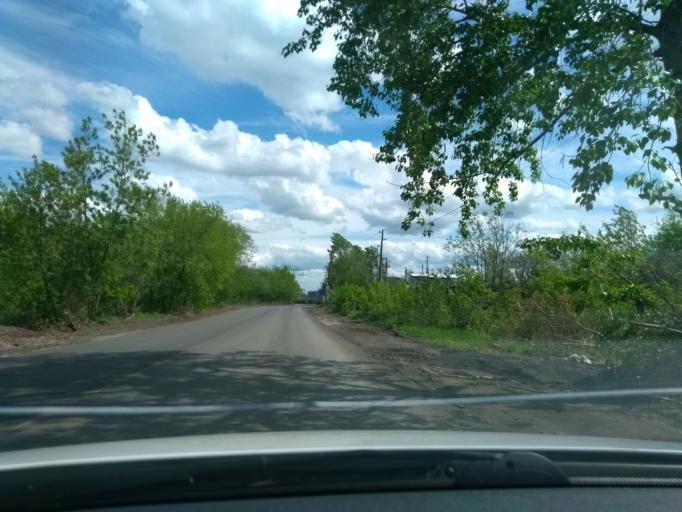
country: RU
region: Perm
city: Kondratovo
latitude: 58.0088
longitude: 56.0834
